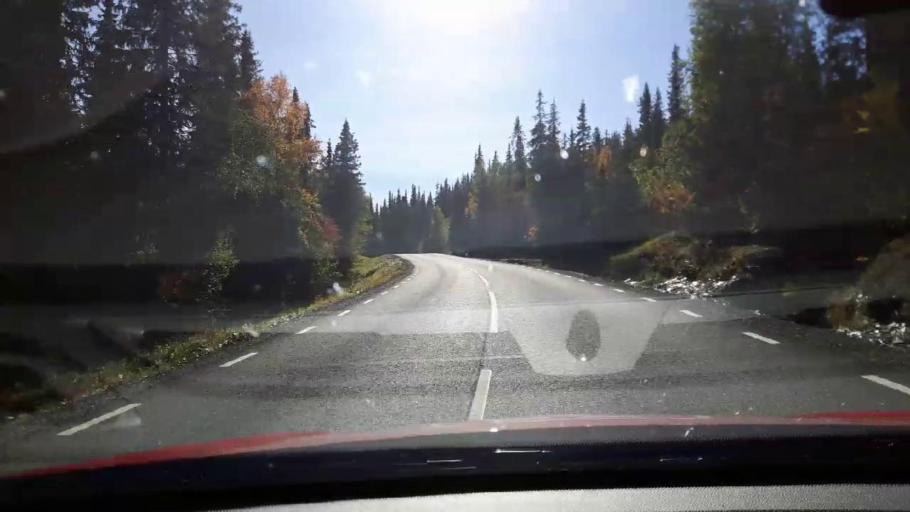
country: NO
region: Nord-Trondelag
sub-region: Royrvik
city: Royrvik
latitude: 64.8600
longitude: 14.1807
